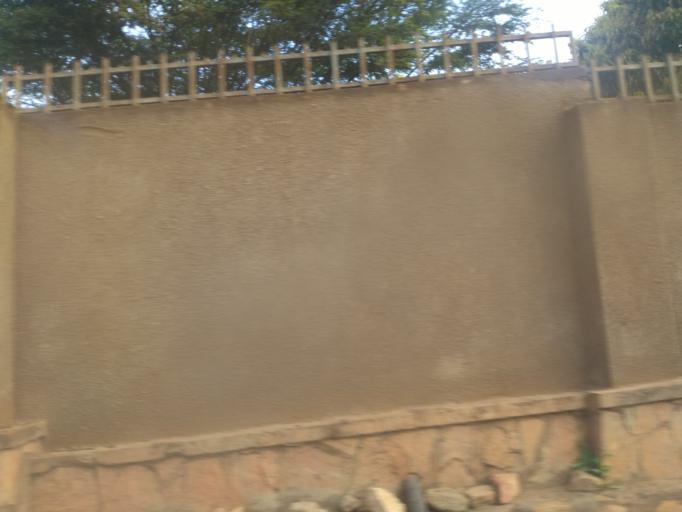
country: UG
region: Central Region
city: Kampala Central Division
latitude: 0.3494
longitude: 32.5939
